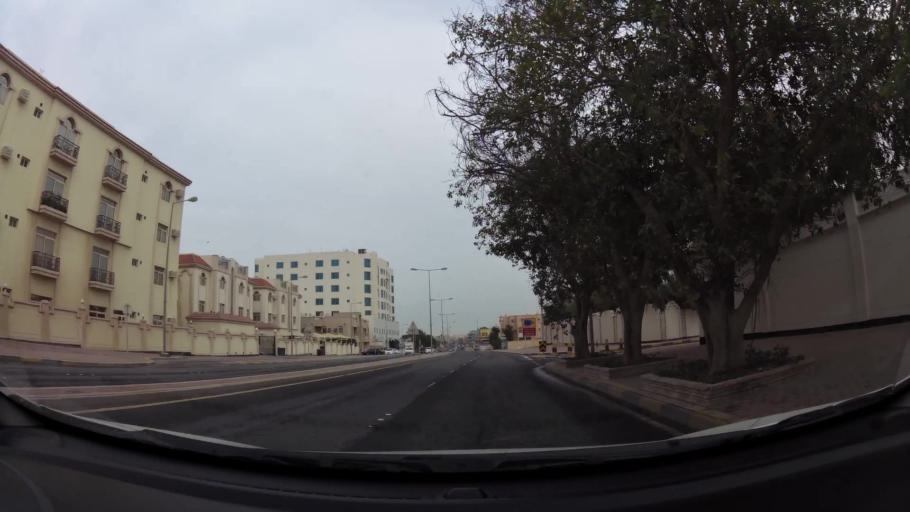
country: BH
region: Northern
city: Ar Rifa'
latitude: 26.1345
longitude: 50.5448
